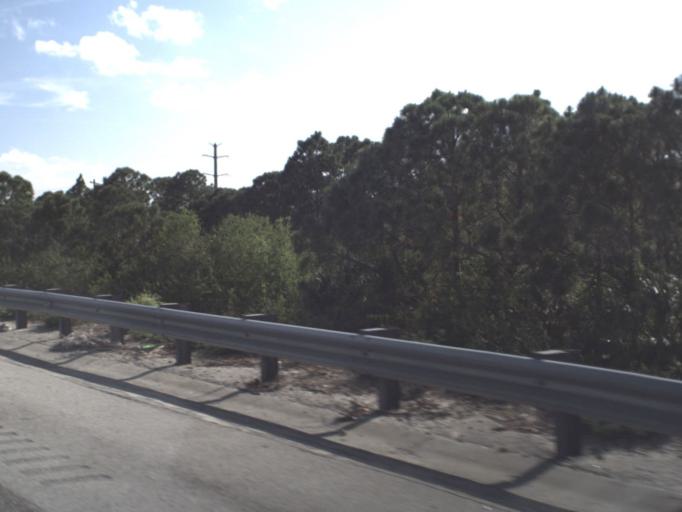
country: US
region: Florida
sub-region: Brevard County
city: June Park
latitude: 28.1458
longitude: -80.7061
